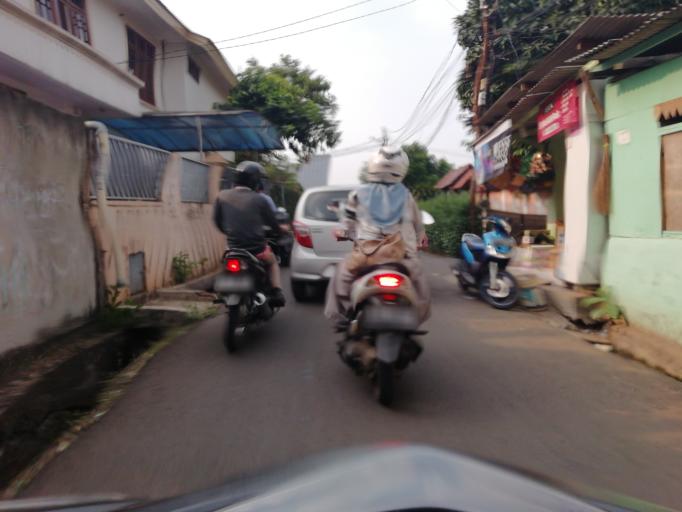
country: ID
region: West Java
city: Pamulang
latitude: -6.3049
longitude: 106.8063
